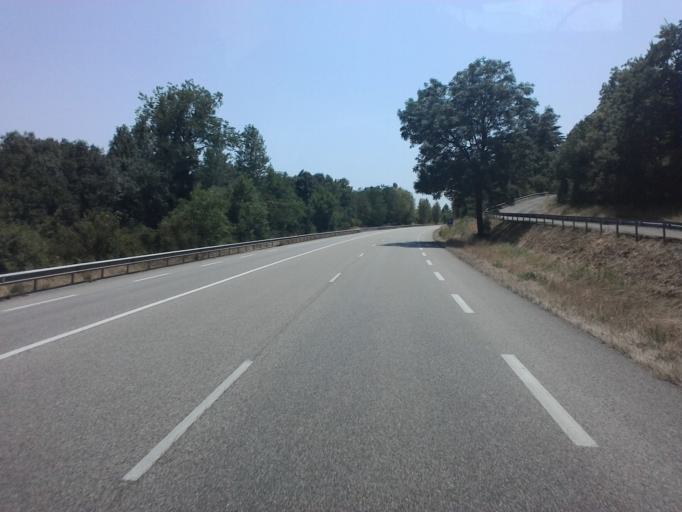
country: FR
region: Rhone-Alpes
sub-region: Departement de l'Ain
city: Lagnieu
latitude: 45.8961
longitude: 5.3380
